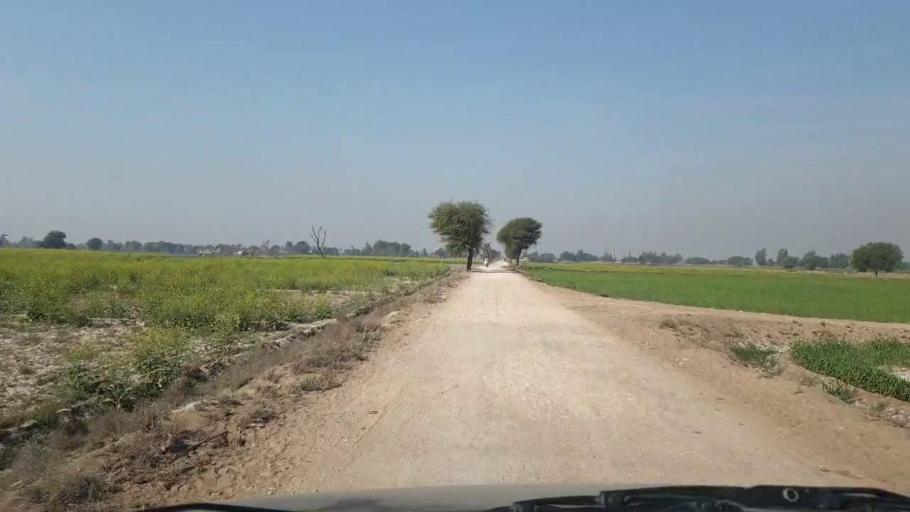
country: PK
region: Sindh
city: Tando Allahyar
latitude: 25.4062
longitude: 68.7292
